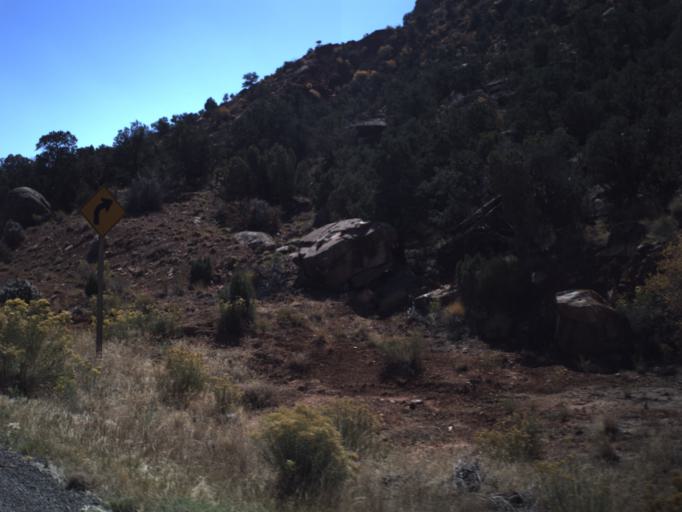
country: US
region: Utah
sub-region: San Juan County
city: Blanding
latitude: 37.5948
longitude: -110.0454
